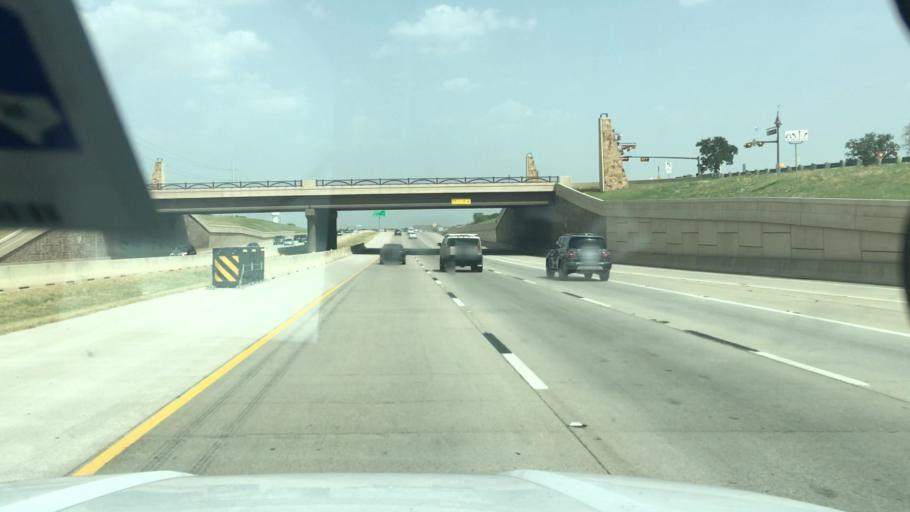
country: US
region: Texas
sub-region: Denton County
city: Trophy Club
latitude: 32.9897
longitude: -97.1829
